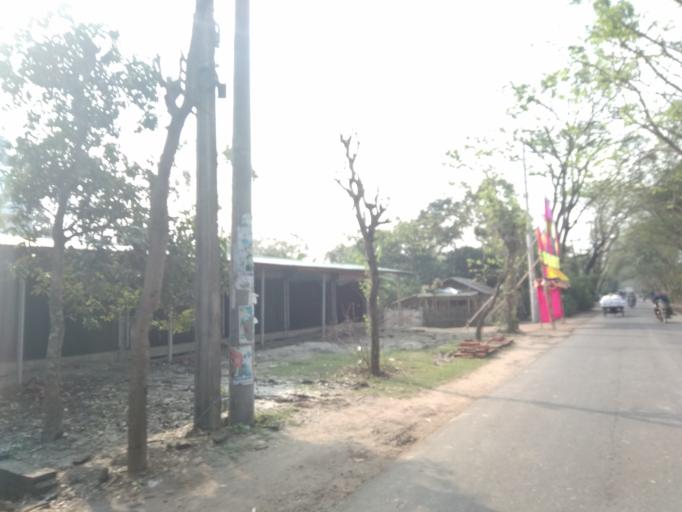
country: IN
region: West Bengal
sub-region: North 24 Parganas
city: Taki
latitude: 22.3252
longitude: 89.1056
